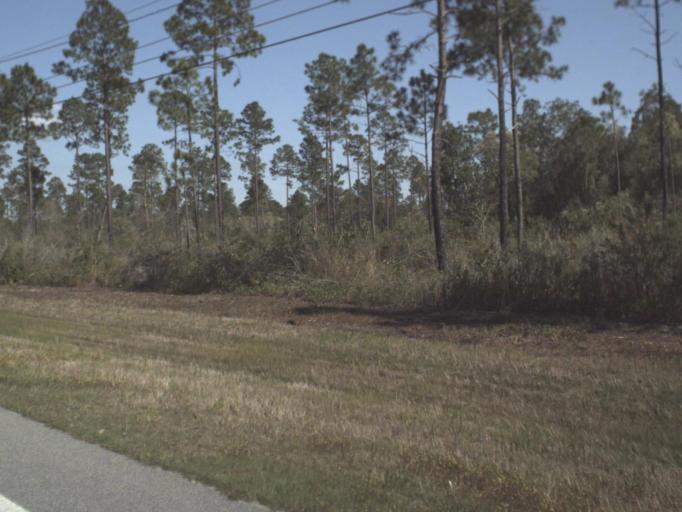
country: US
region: Florida
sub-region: Bay County
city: Panama City Beach
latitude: 30.3226
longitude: -85.7956
